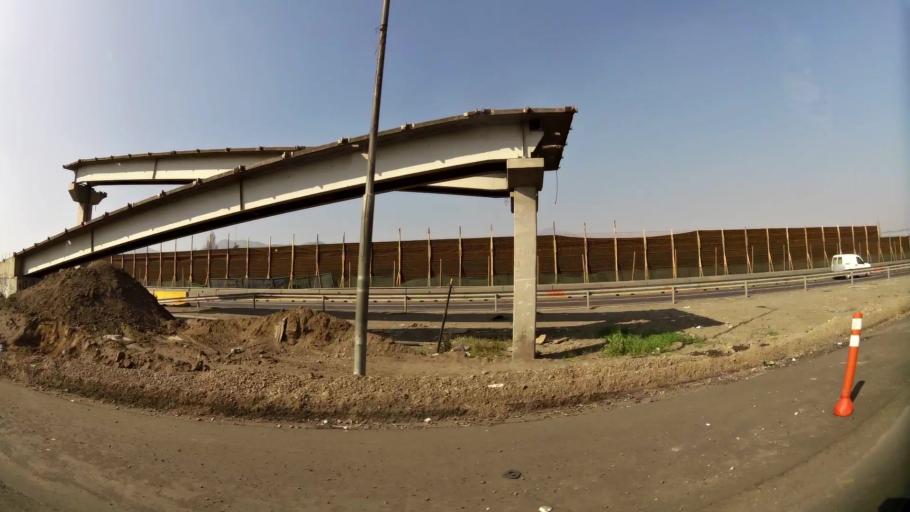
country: CL
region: Santiago Metropolitan
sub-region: Provincia de Santiago
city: Lo Prado
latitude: -33.3592
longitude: -70.7038
